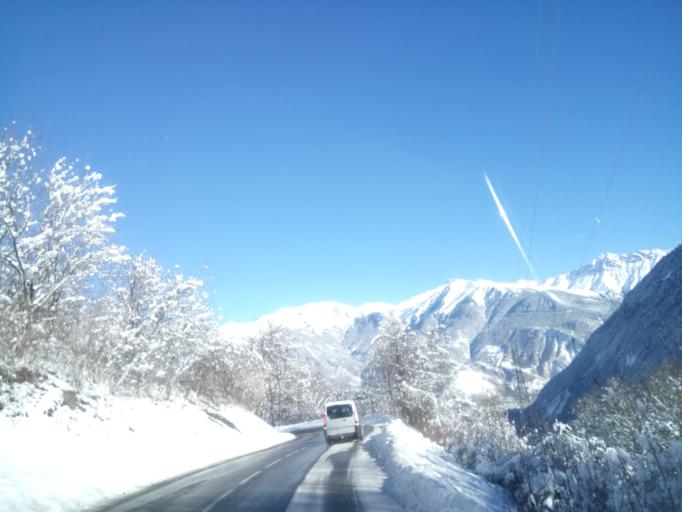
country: FR
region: Rhone-Alpes
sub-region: Departement de la Savoie
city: Saint-Jean-de-Maurienne
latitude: 45.2490
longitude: 6.3127
